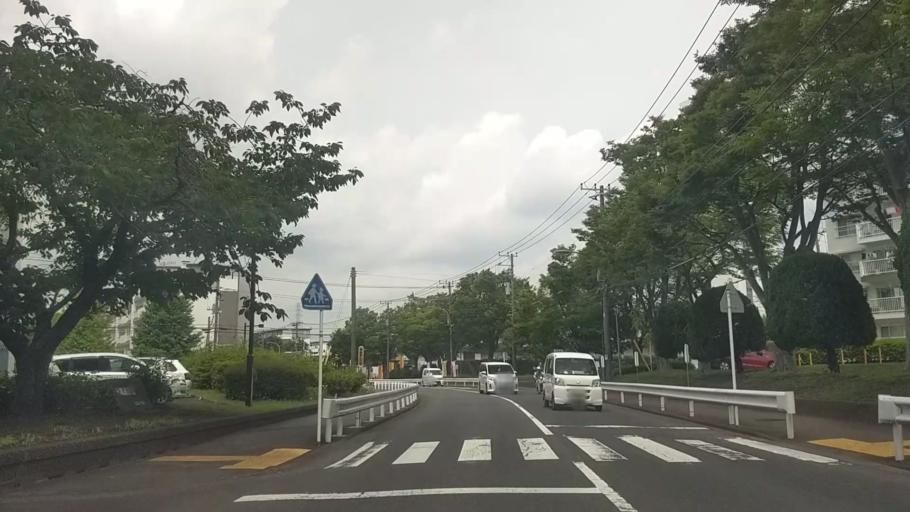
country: JP
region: Kanagawa
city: Fujisawa
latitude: 35.3666
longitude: 139.4660
